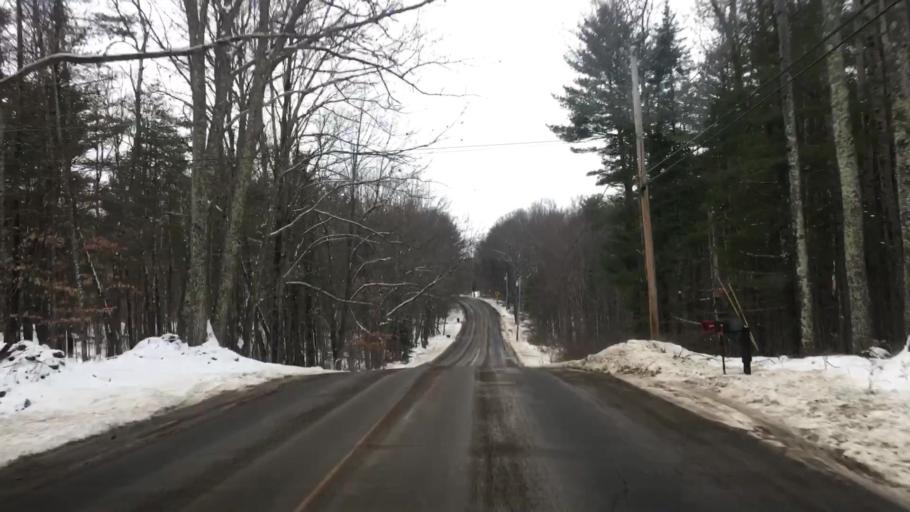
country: US
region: Maine
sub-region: Lincoln County
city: Whitefield
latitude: 44.2466
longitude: -69.6332
